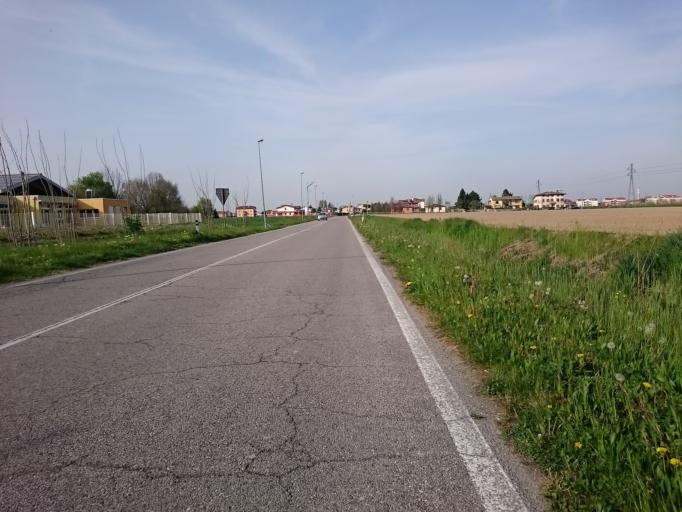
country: IT
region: Veneto
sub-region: Provincia di Padova
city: Masera di Padova
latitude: 45.3329
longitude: 11.8690
